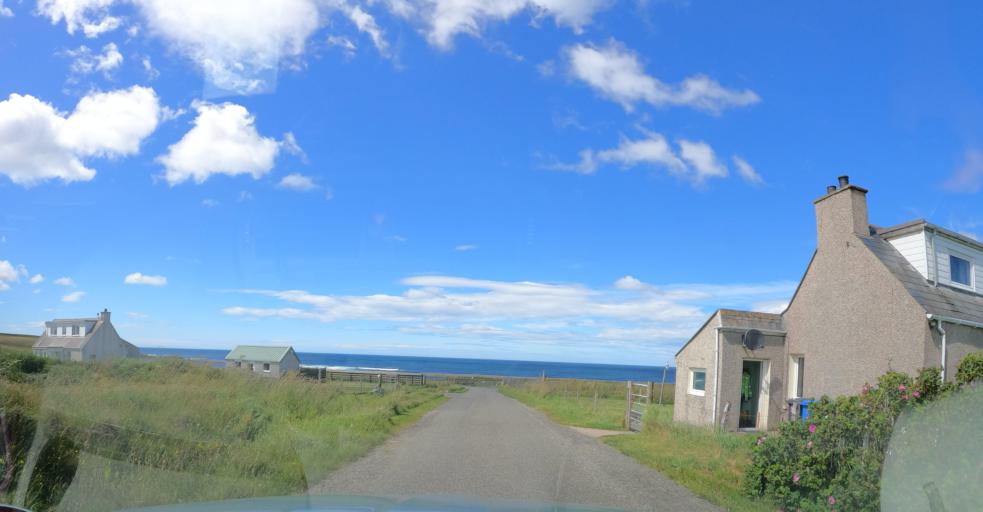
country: GB
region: Scotland
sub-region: Eilean Siar
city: Isle of Lewis
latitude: 58.3606
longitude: -6.5622
